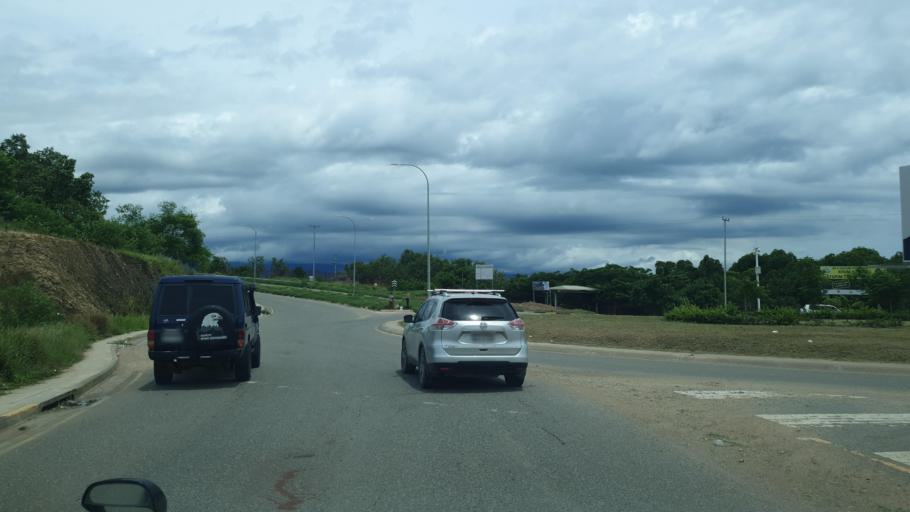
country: PG
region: National Capital
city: Port Moresby
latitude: -9.5004
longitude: 147.2342
